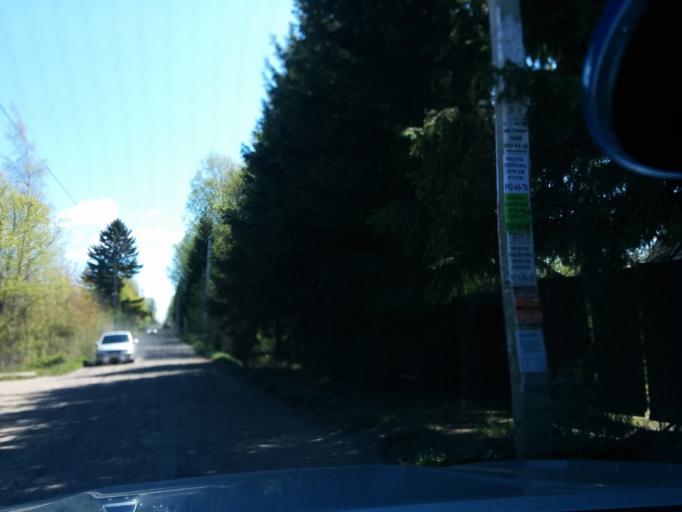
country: RU
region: Leningrad
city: Verkhniye Osel'ki
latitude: 60.2573
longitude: 30.4319
